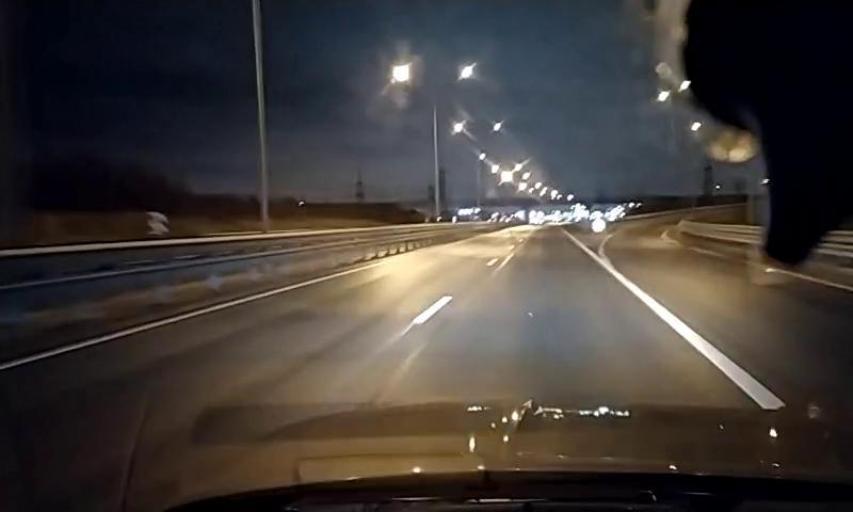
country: RU
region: Leningrad
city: Bugry
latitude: 60.1029
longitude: 30.3850
